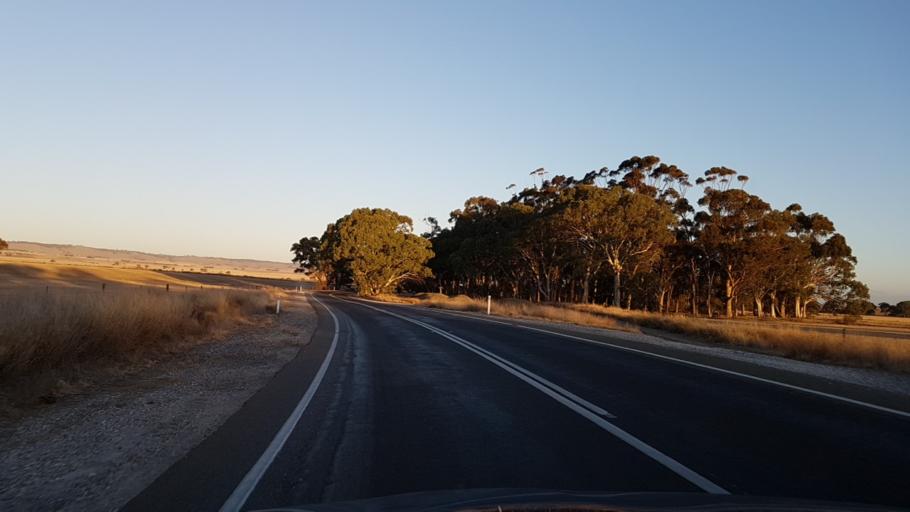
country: AU
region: South Australia
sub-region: Light
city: Kapunda
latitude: -34.2283
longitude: 138.7349
